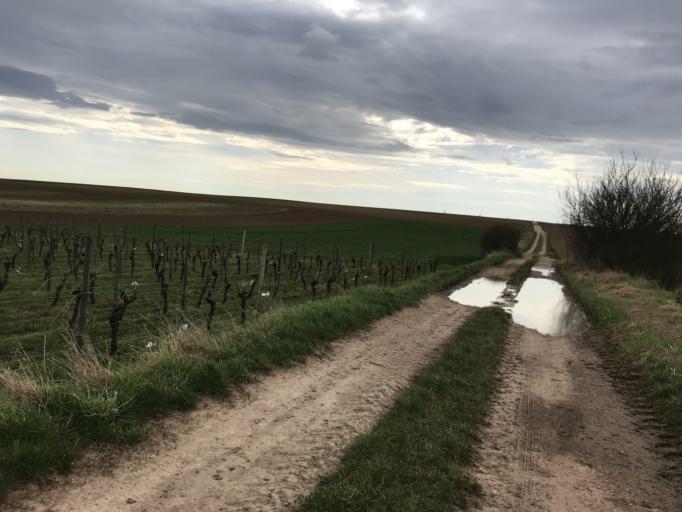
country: DE
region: Rheinland-Pfalz
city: Stadecken-Elsheim
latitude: 49.8920
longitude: 8.1385
